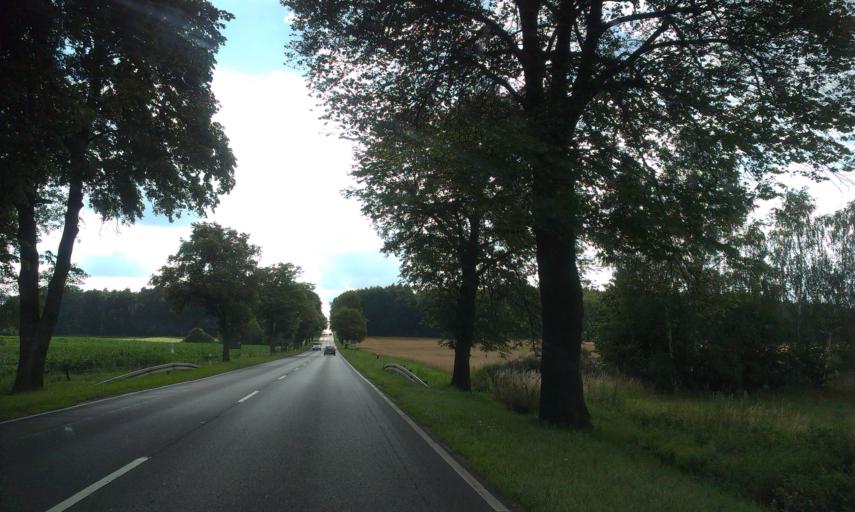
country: PL
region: Greater Poland Voivodeship
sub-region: Powiat pilski
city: Miasteczko Krajenskie
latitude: 53.1327
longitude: 16.9951
